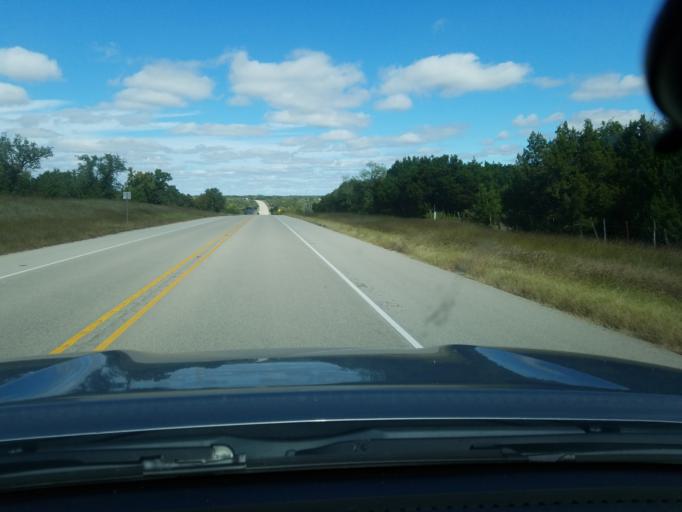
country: US
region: Texas
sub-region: Hamilton County
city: Hamilton
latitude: 31.5770
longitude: -98.1577
